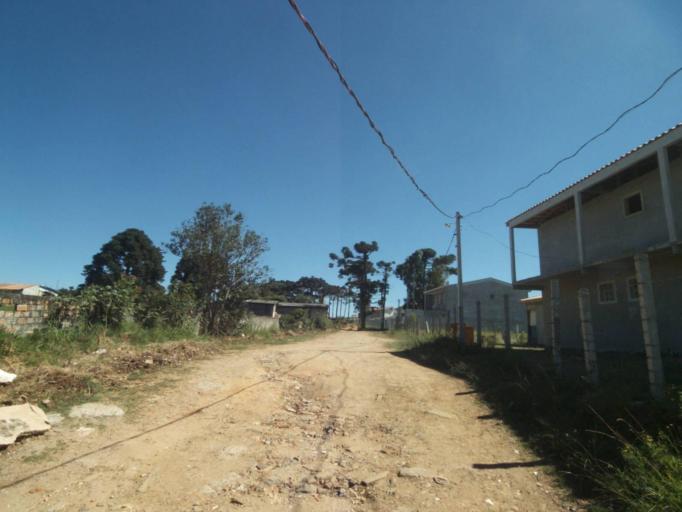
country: BR
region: Parana
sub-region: Curitiba
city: Curitiba
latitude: -25.4892
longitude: -49.3397
